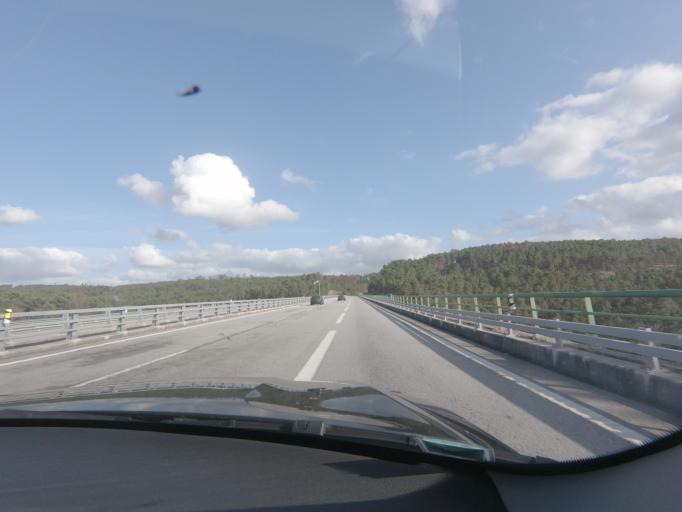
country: PT
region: Viseu
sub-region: Viseu
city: Campo
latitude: 40.7745
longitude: -7.9261
